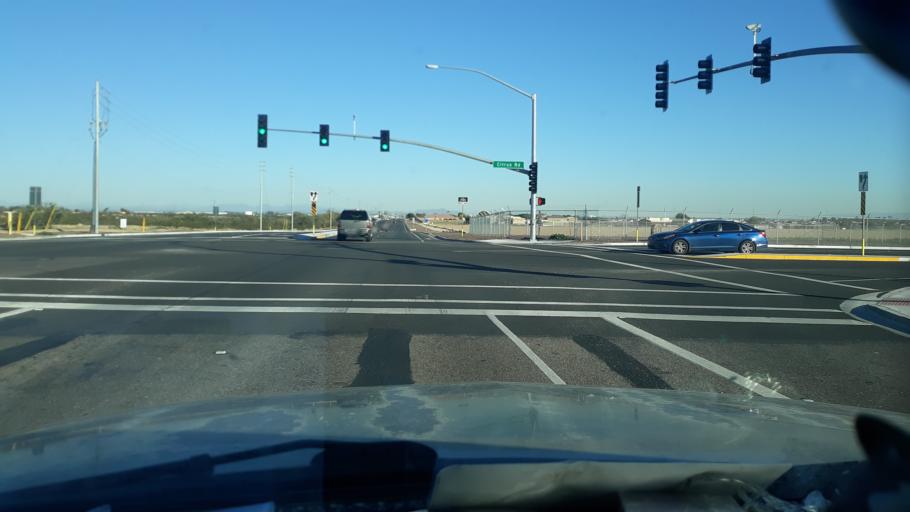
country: US
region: Arizona
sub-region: Maricopa County
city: Citrus Park
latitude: 33.5661
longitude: -112.4447
